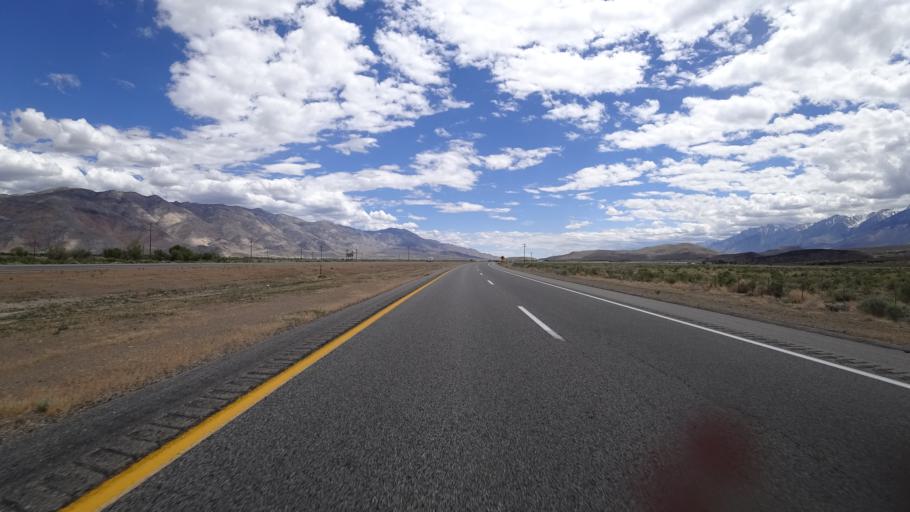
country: US
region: California
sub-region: Inyo County
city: Big Pine
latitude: 37.1106
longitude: -118.2555
